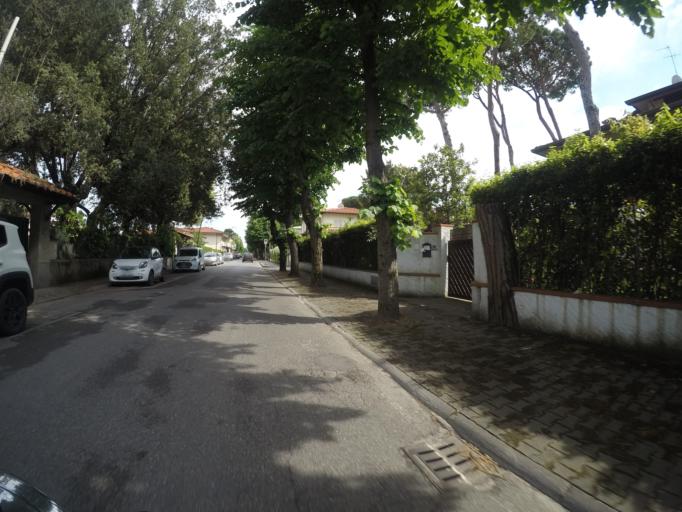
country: IT
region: Tuscany
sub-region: Provincia di Lucca
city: Forte dei Marmi
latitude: 43.9707
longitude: 10.1554
